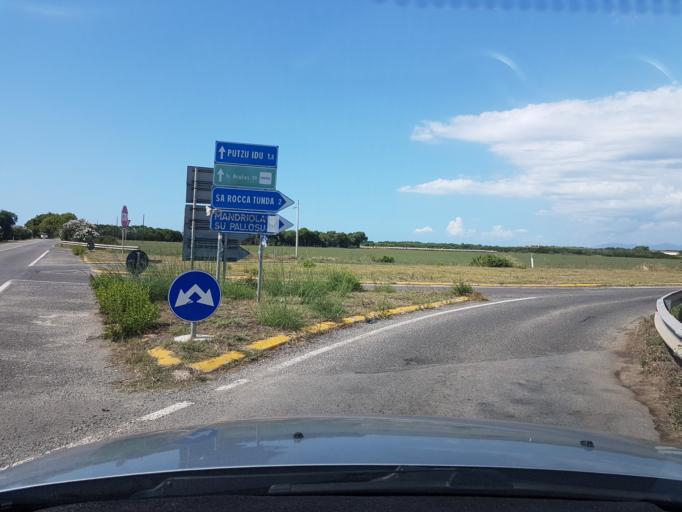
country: IT
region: Sardinia
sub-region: Provincia di Oristano
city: Riola Sardo
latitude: 40.0259
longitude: 8.4295
